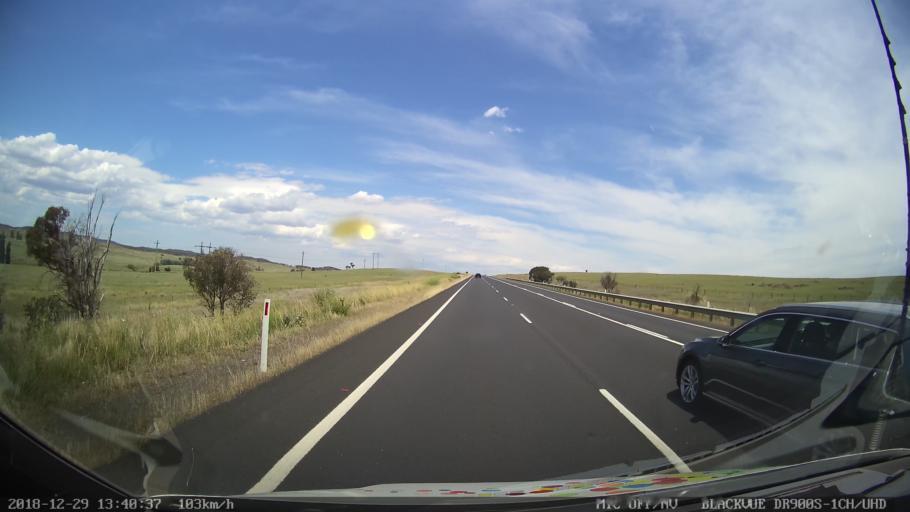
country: AU
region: New South Wales
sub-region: Cooma-Monaro
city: Cooma
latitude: -36.0297
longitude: 149.1532
